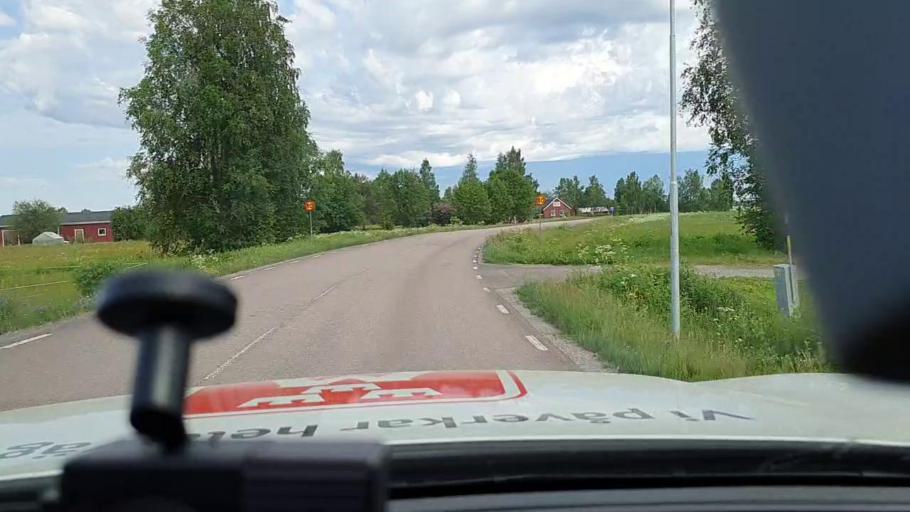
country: SE
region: Norrbotten
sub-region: Bodens Kommun
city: Saevast
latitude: 65.6860
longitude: 21.7857
